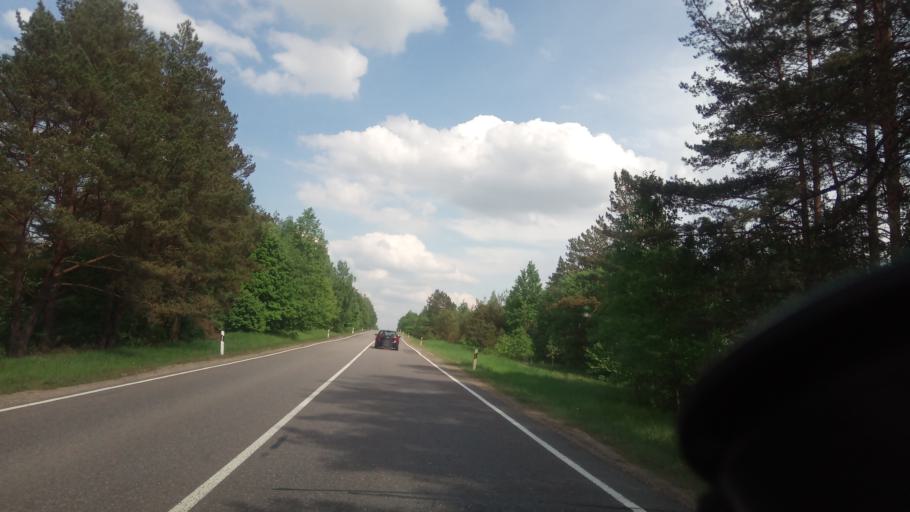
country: LT
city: Trakai
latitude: 54.6074
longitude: 24.8540
